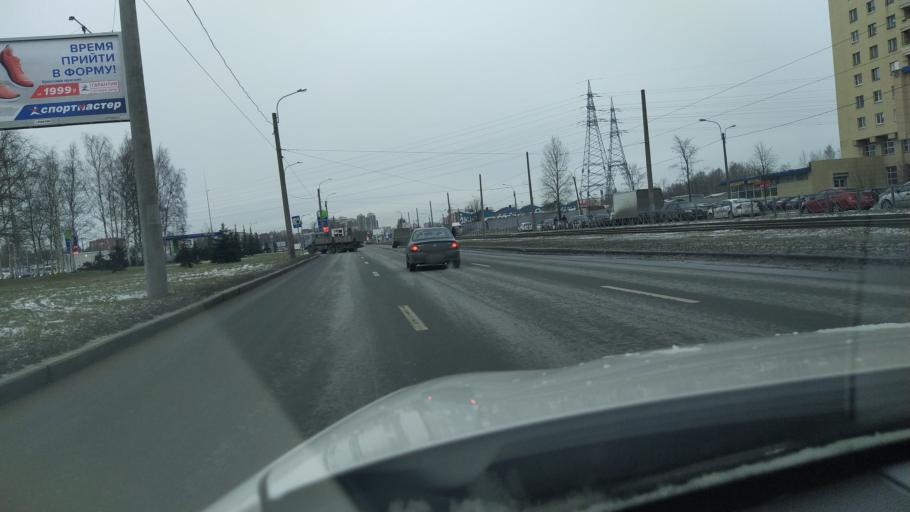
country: RU
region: St.-Petersburg
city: Grazhdanka
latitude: 60.0136
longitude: 30.4337
